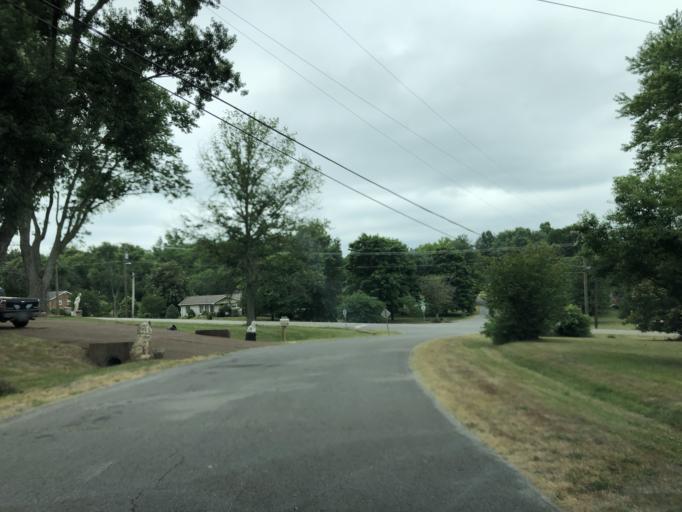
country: US
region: Tennessee
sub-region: Davidson County
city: Goodlettsville
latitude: 36.2801
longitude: -86.7629
